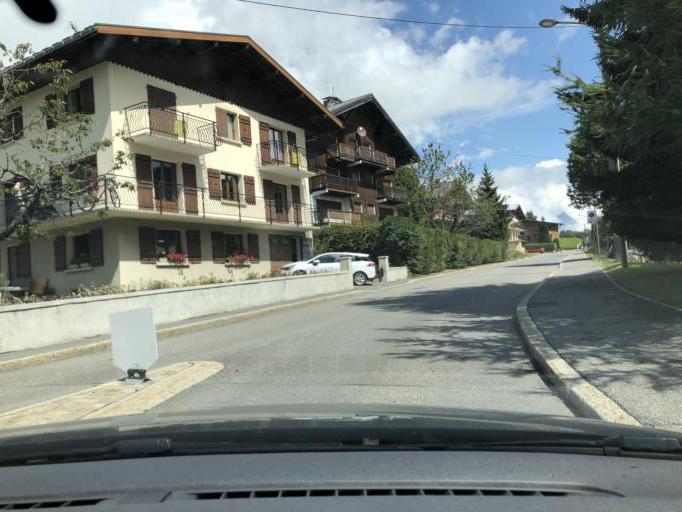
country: FR
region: Rhone-Alpes
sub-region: Departement de la Haute-Savoie
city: Megeve
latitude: 45.8622
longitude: 6.6183
